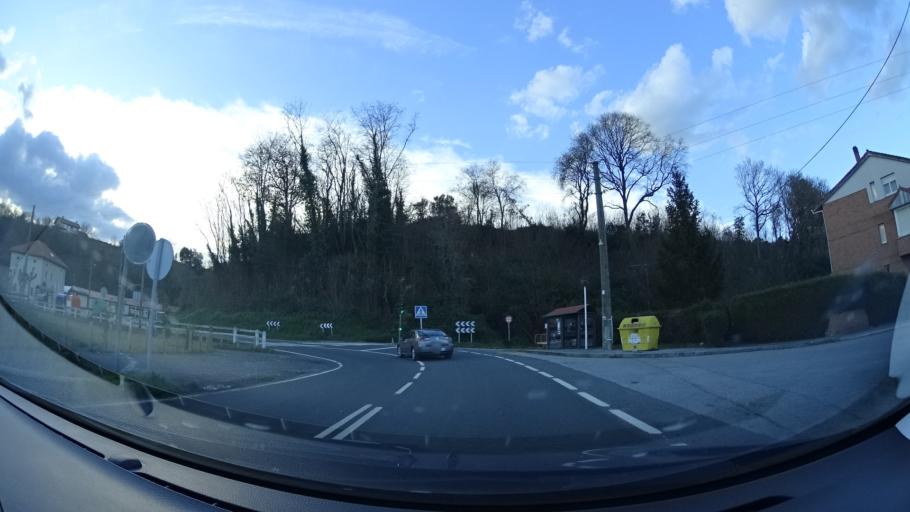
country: ES
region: Basque Country
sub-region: Bizkaia
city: Plentzia
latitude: 43.4040
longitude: -2.9532
